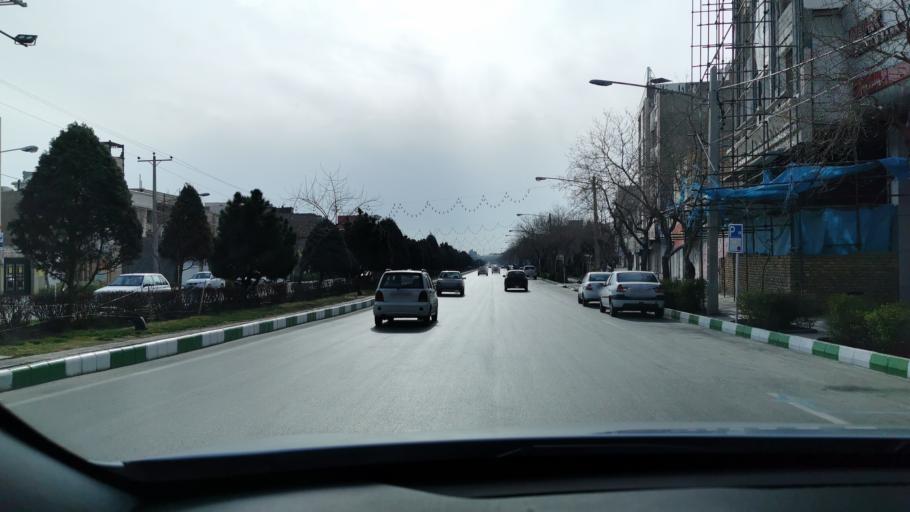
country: IR
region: Razavi Khorasan
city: Mashhad
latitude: 36.3044
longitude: 59.5132
